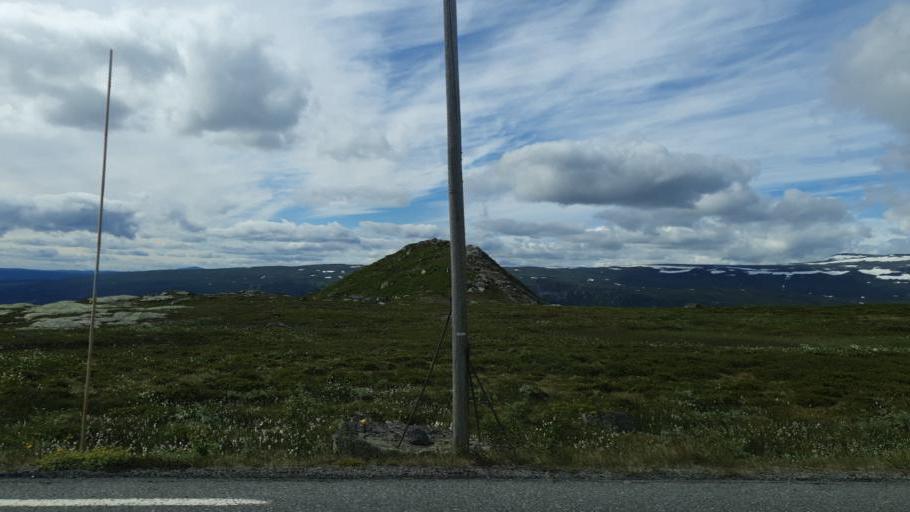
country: NO
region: Oppland
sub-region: Vestre Slidre
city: Slidre
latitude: 61.2828
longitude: 8.8333
